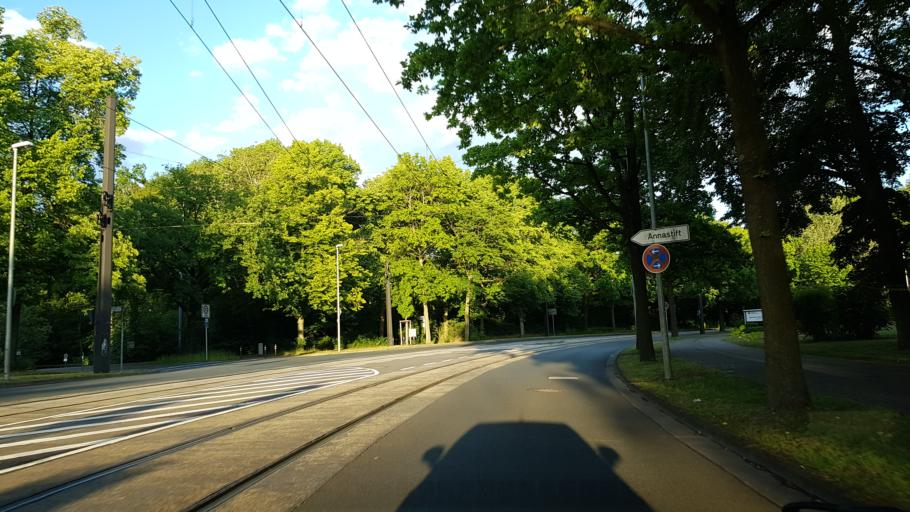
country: DE
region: Lower Saxony
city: Laatzen
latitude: 52.3693
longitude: 9.8087
